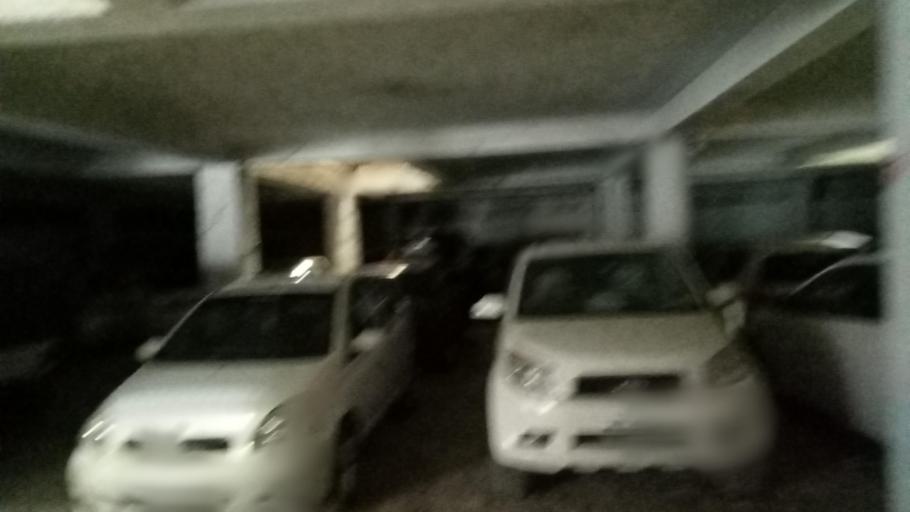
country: PK
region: Khyber Pakhtunkhwa
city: Mingora
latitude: 34.7715
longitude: 72.3631
